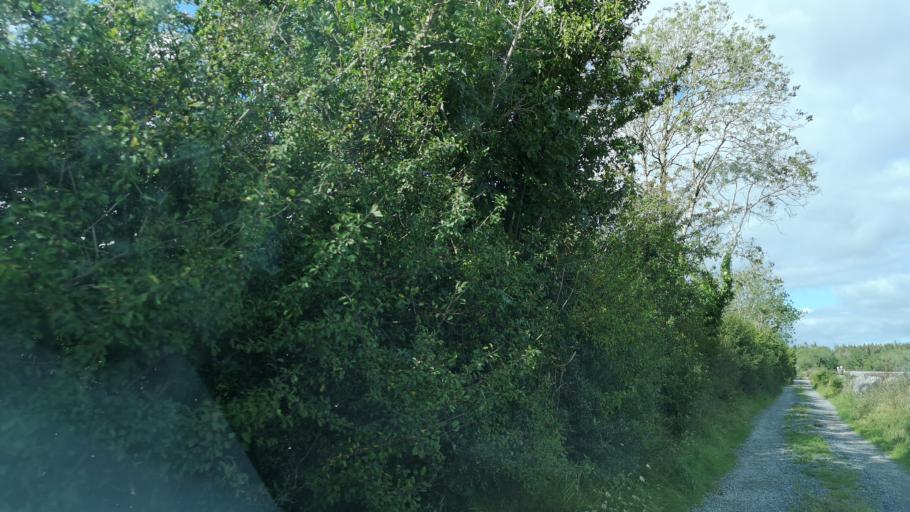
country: IE
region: Connaught
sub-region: County Galway
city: Moycullen
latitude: 53.3564
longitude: -9.1569
